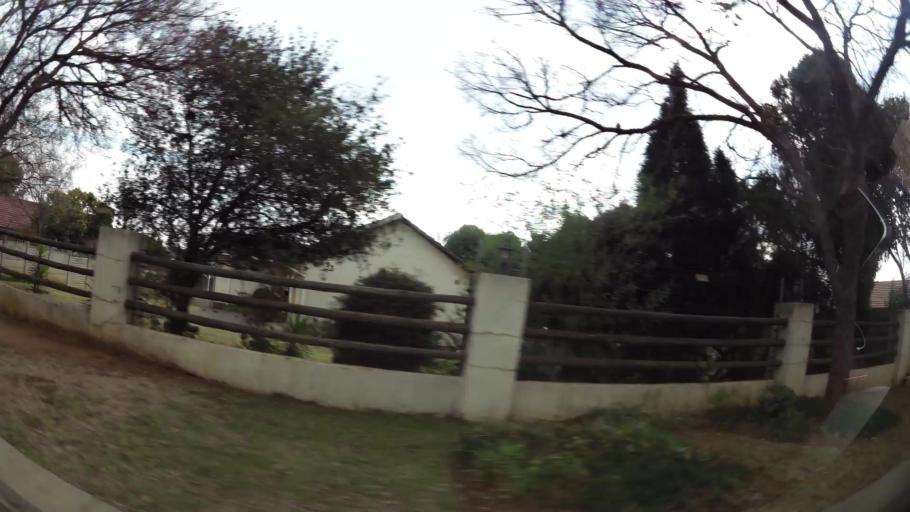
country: ZA
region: Gauteng
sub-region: Ekurhuleni Metropolitan Municipality
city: Benoni
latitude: -26.1263
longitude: 28.3618
